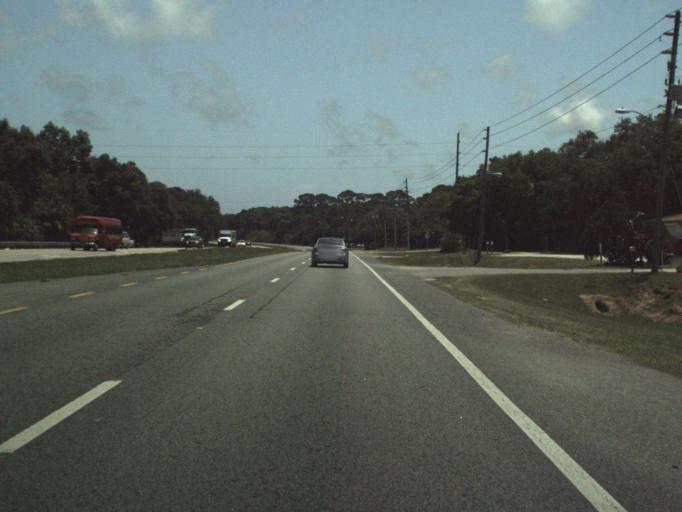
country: US
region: Florida
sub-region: Volusia County
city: Ormond Beach
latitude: 29.3043
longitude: -81.0934
